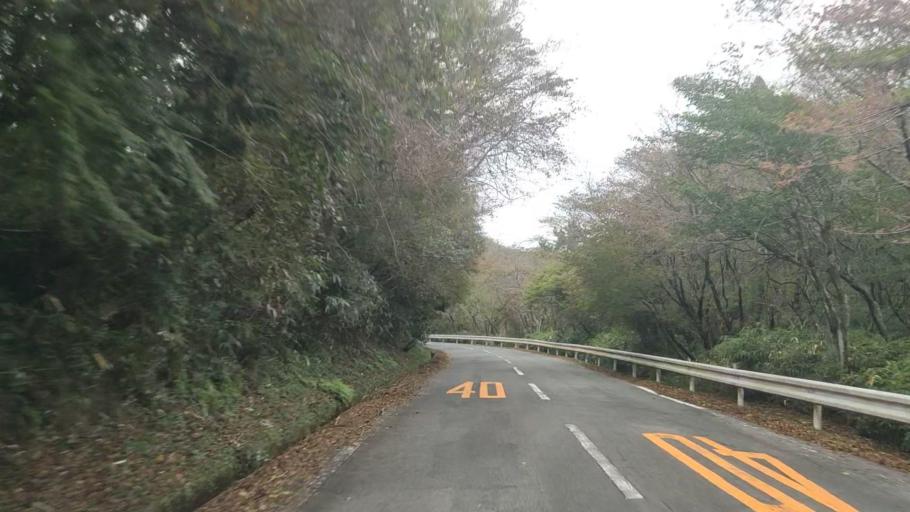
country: JP
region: Shizuoka
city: Heda
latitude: 34.9306
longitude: 138.8403
